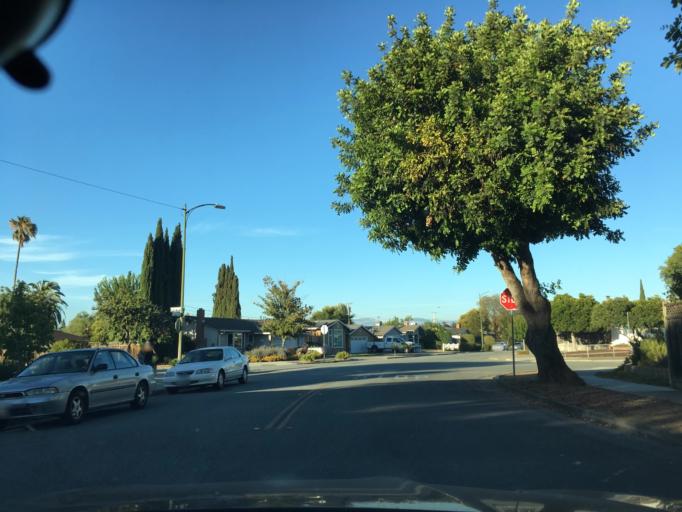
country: US
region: California
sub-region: Santa Clara County
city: Cambrian Park
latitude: 37.2336
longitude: -121.9065
